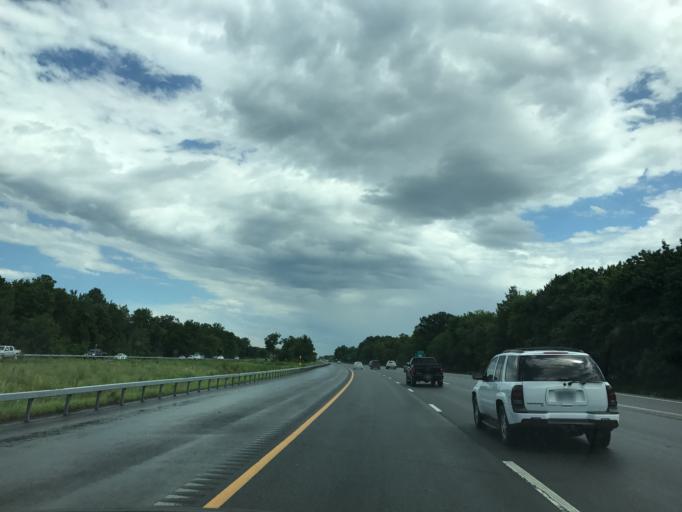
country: US
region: New York
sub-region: Albany County
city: Roessleville
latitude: 42.7310
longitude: -73.7905
